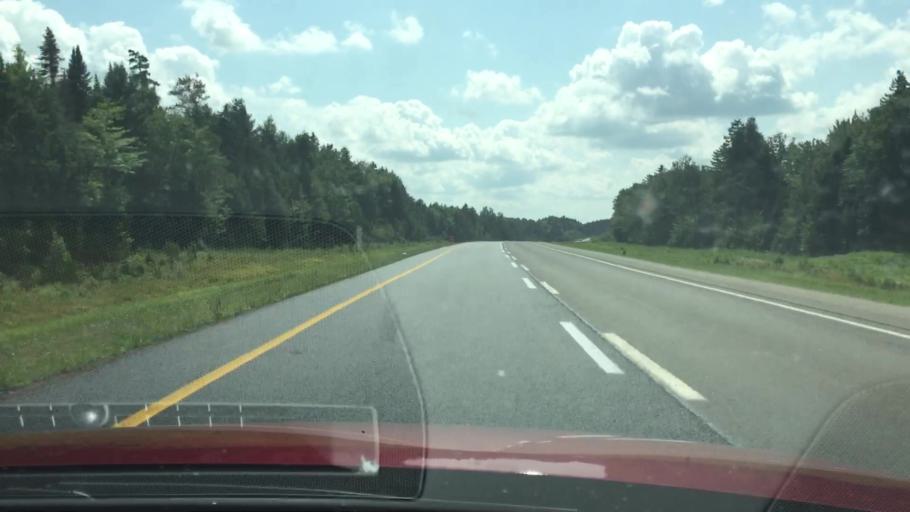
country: US
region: Maine
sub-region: Penobscot County
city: Medway
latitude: 45.6920
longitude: -68.4882
